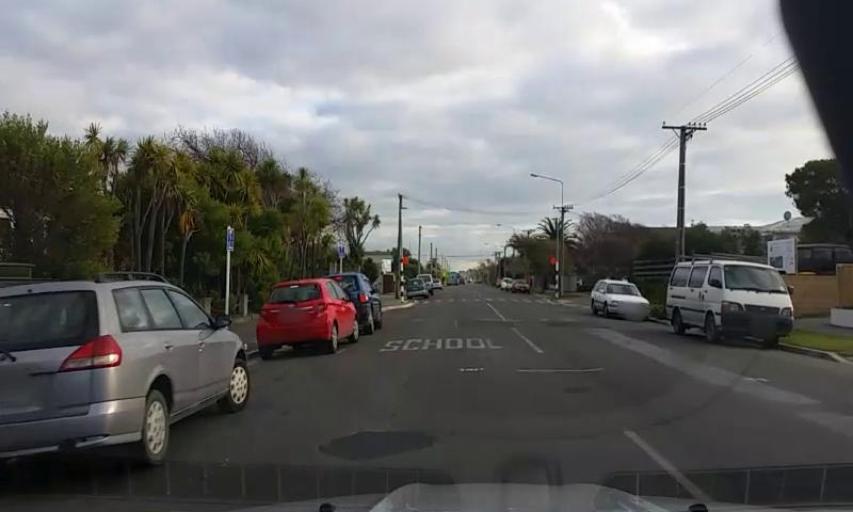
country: NZ
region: Canterbury
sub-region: Christchurch City
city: Christchurch
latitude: -43.5267
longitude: 172.7341
